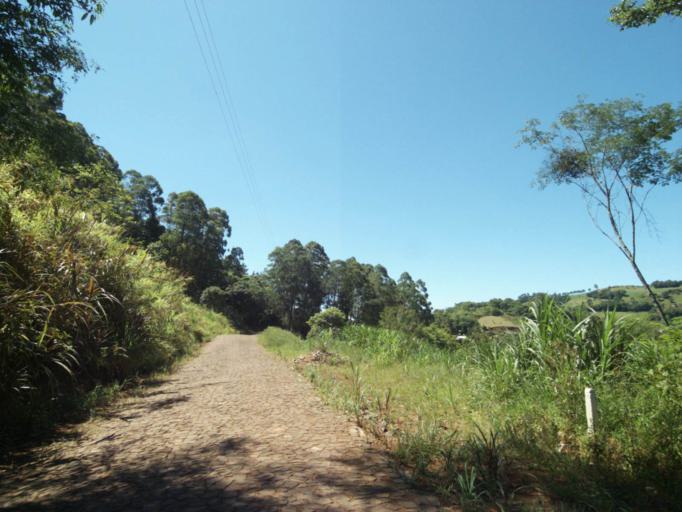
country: BR
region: Parana
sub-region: Ampere
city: Ampere
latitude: -26.1809
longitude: -53.3592
